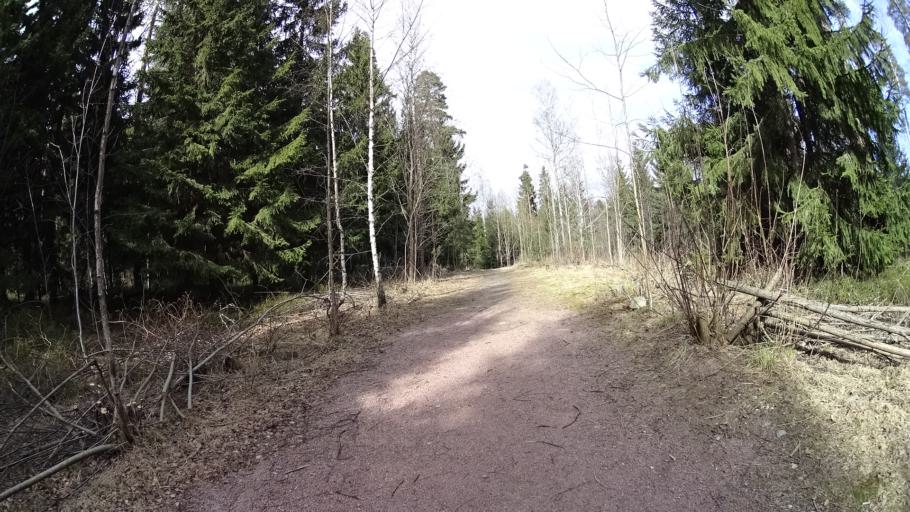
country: FI
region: Uusimaa
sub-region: Helsinki
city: Kauniainen
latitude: 60.2161
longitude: 24.7478
